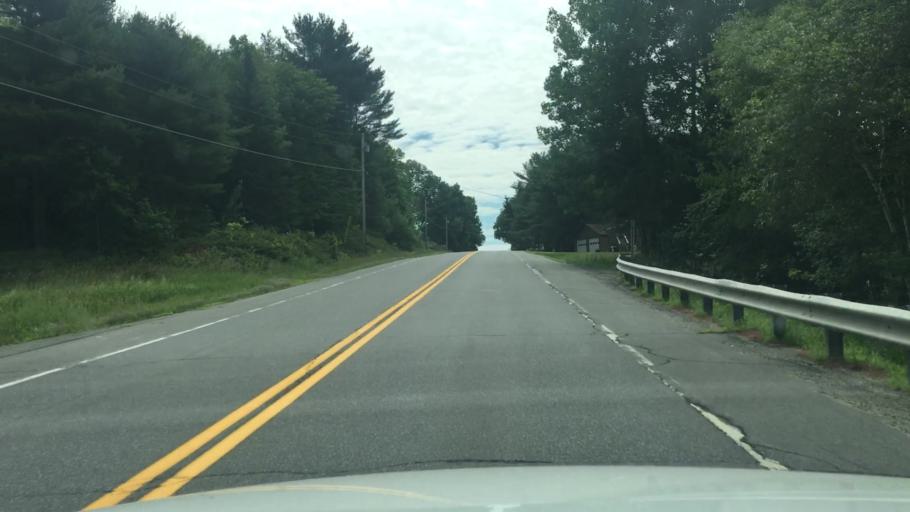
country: US
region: Maine
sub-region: Waldo County
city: Troy
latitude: 44.6032
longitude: -69.2949
